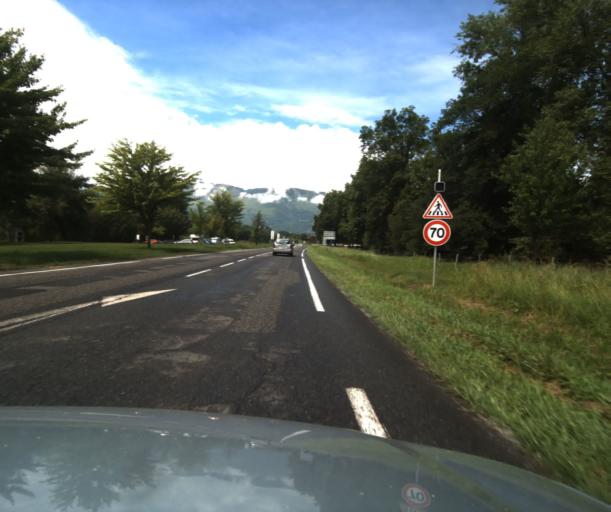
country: FR
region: Midi-Pyrenees
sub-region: Departement des Hautes-Pyrenees
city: Pierrefitte-Nestalas
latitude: 42.9923
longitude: -0.0757
